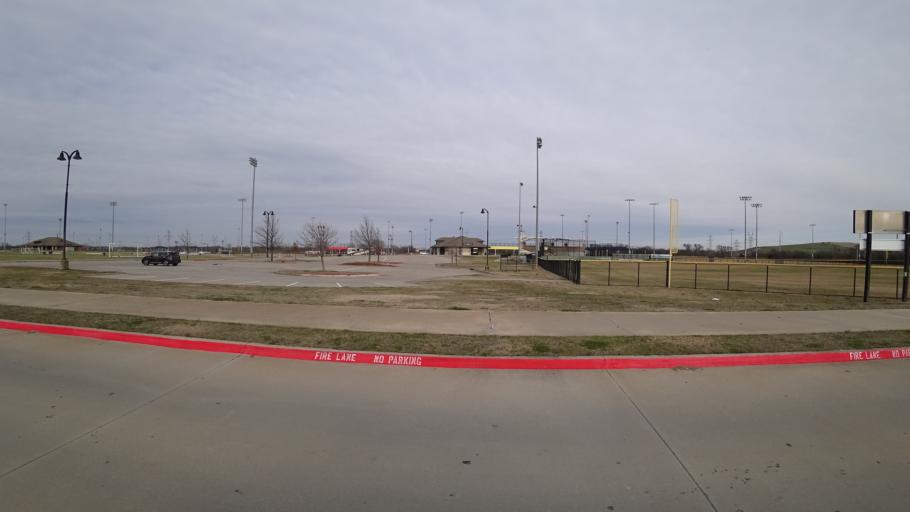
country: US
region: Texas
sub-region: Denton County
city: Lewisville
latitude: 33.0286
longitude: -96.9714
